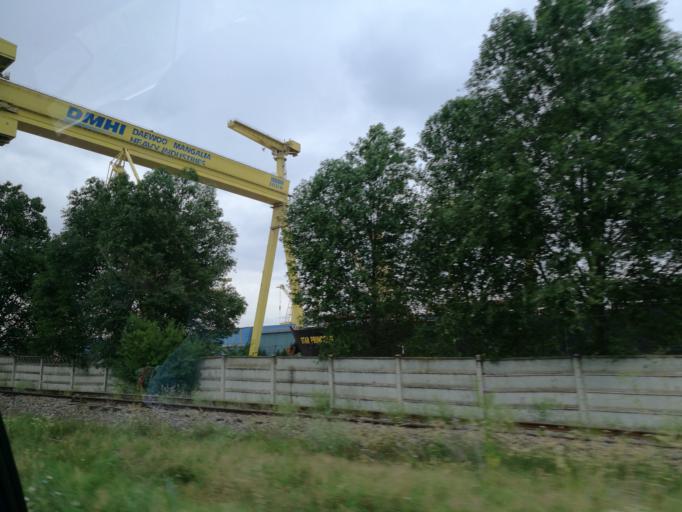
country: RO
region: Constanta
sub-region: Municipiul Mangalia
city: Mangalia
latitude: 43.7947
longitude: 28.5725
